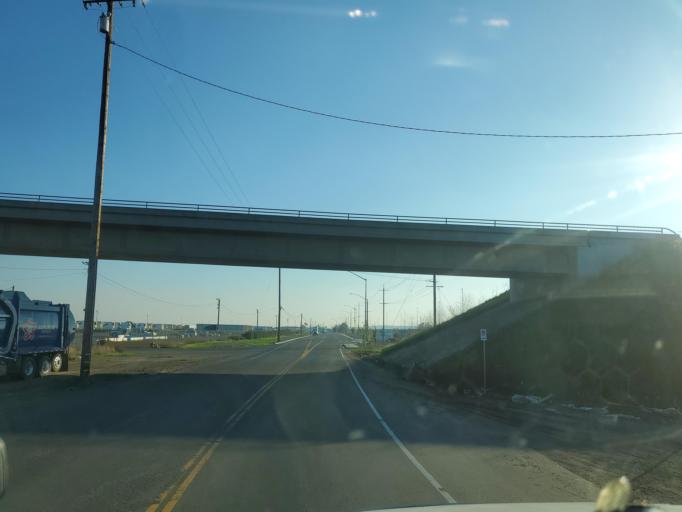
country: US
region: California
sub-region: San Joaquin County
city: Garden Acres
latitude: 37.9124
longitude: -121.1842
